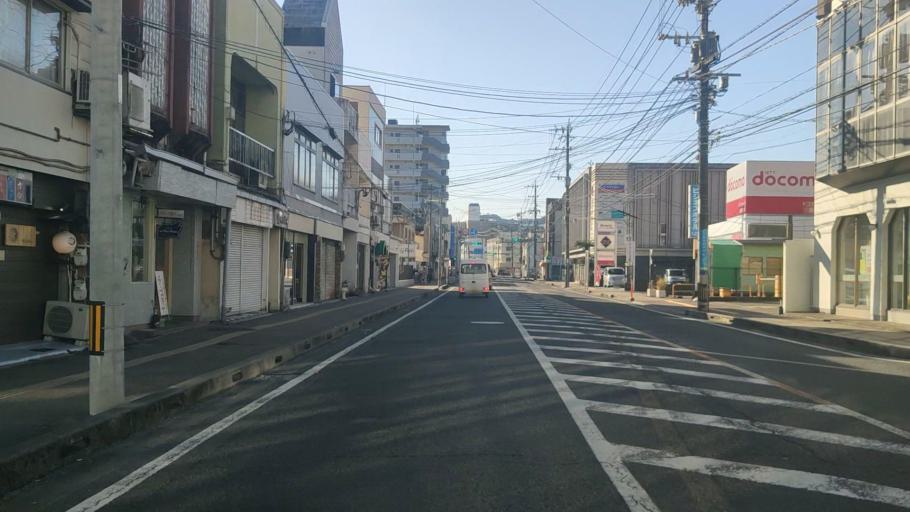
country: JP
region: Miyazaki
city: Nobeoka
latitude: 32.5891
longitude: 131.6712
